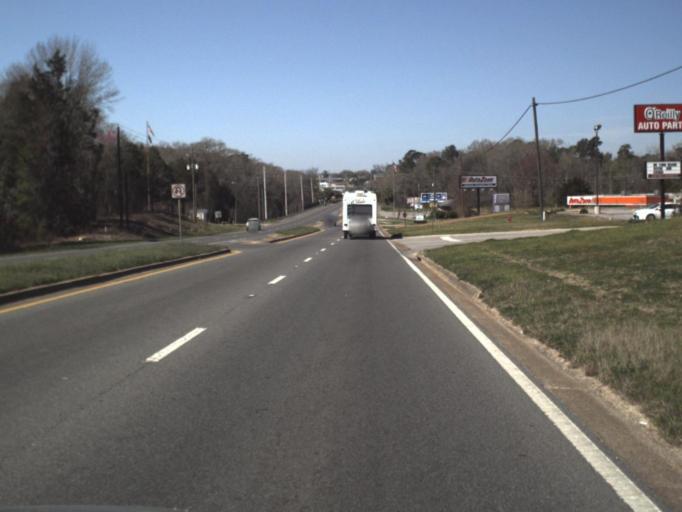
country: US
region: Florida
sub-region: Jackson County
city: Marianna
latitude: 30.7713
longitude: -85.2100
